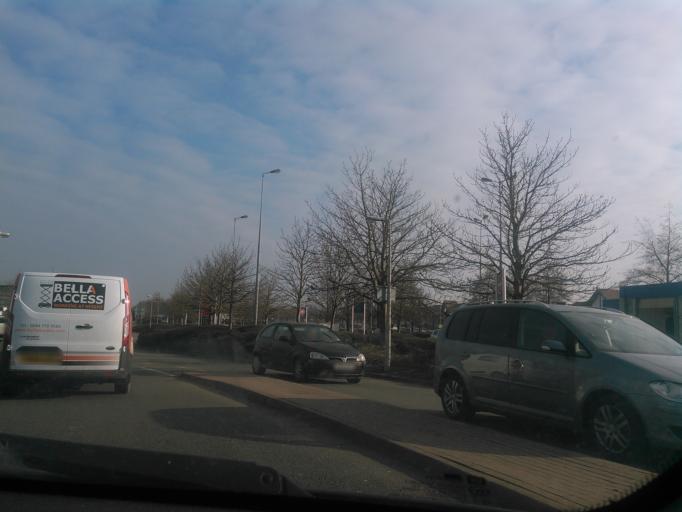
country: GB
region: England
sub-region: Shropshire
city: Bayston Hill
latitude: 52.6872
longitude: -2.7548
